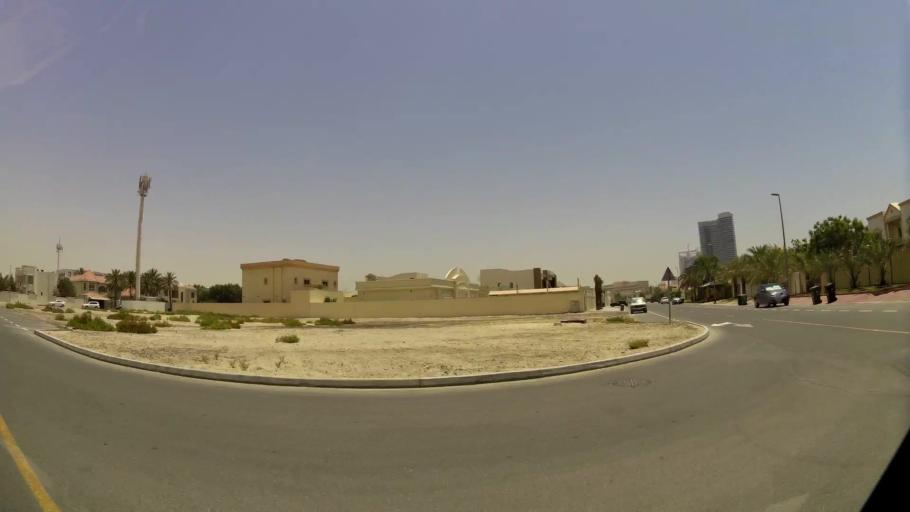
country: AE
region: Dubai
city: Dubai
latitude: 25.1019
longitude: 55.1877
